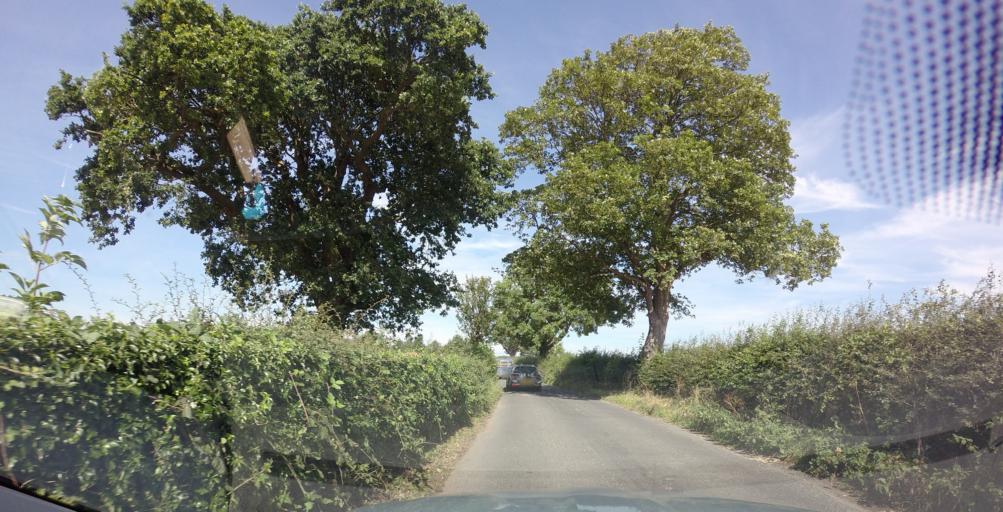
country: GB
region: England
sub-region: North Yorkshire
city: Ripon
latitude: 54.1255
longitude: -1.4865
